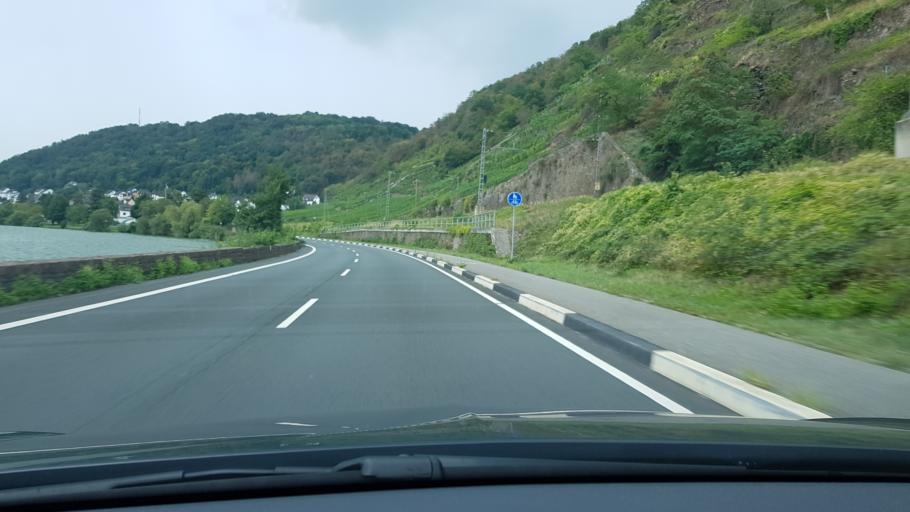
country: DE
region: Rheinland-Pfalz
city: Oberfell
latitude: 50.2585
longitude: 7.4398
